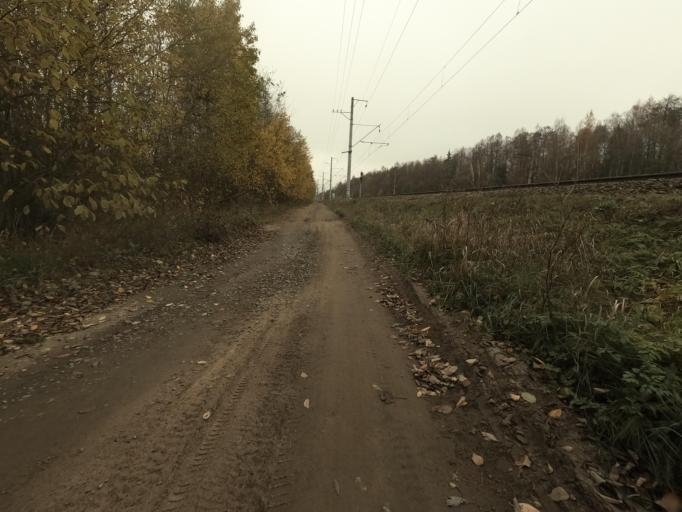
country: RU
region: Leningrad
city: Pavlovo
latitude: 59.7862
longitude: 30.8909
